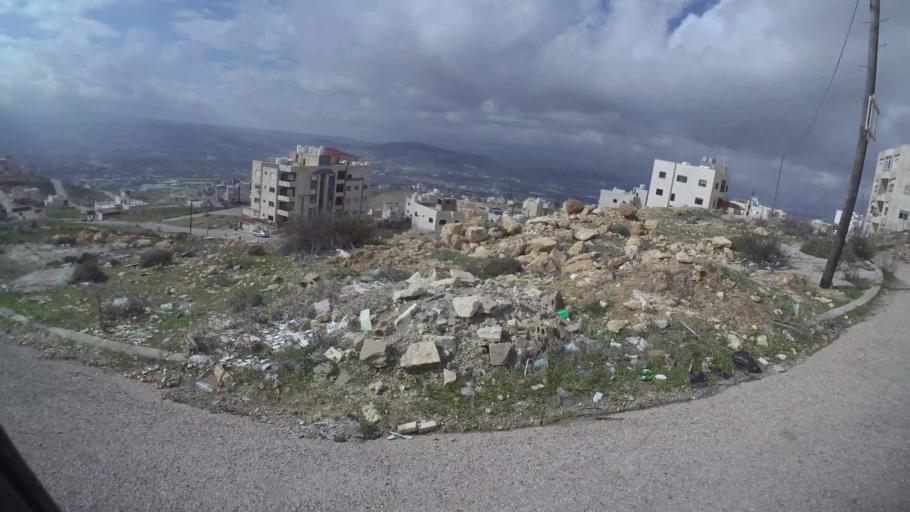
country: JO
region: Amman
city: Al Jubayhah
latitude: 32.0583
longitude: 35.8675
